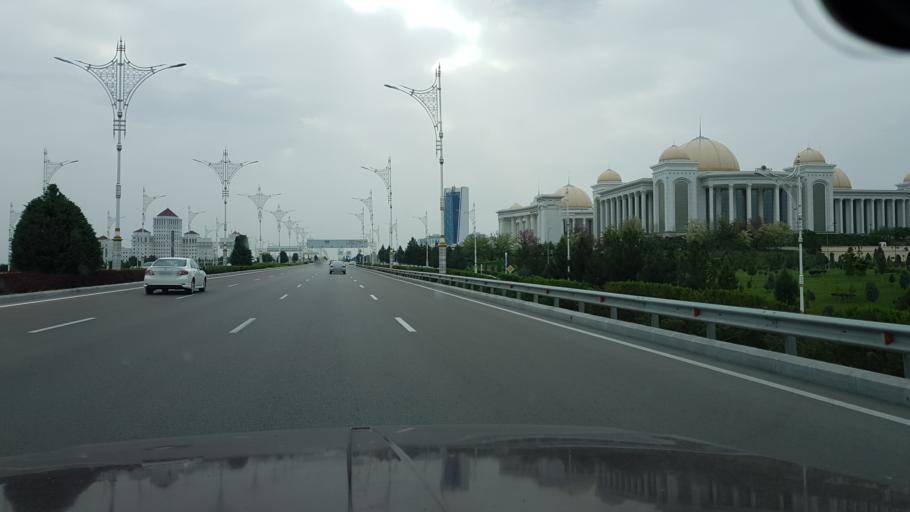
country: TM
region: Ahal
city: Ashgabat
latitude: 37.8789
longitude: 58.3778
